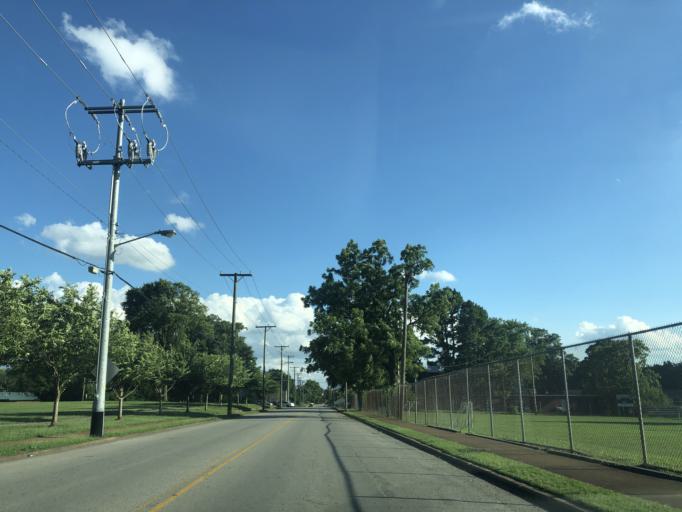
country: US
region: Tennessee
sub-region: Davidson County
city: Nashville
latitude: 36.1825
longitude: -86.7687
